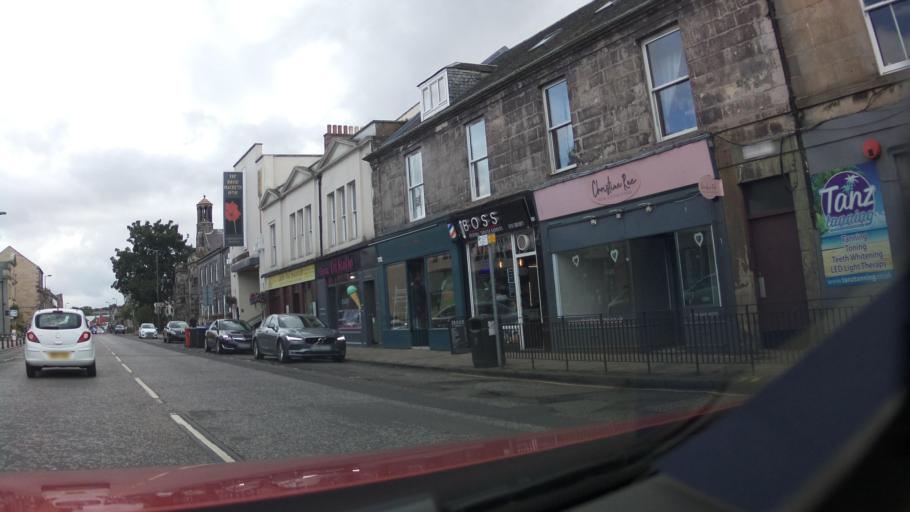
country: GB
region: Scotland
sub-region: East Lothian
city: Musselburgh
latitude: 55.9442
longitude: -3.0588
